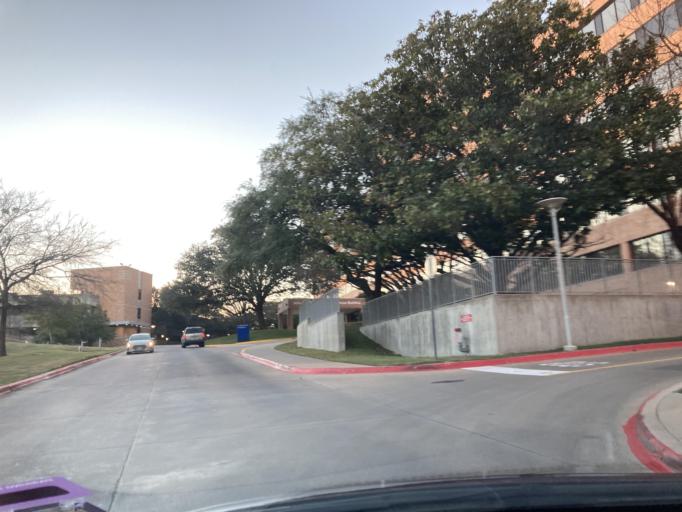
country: US
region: Texas
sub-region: Dallas County
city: University Park
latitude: 32.8800
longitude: -96.7628
